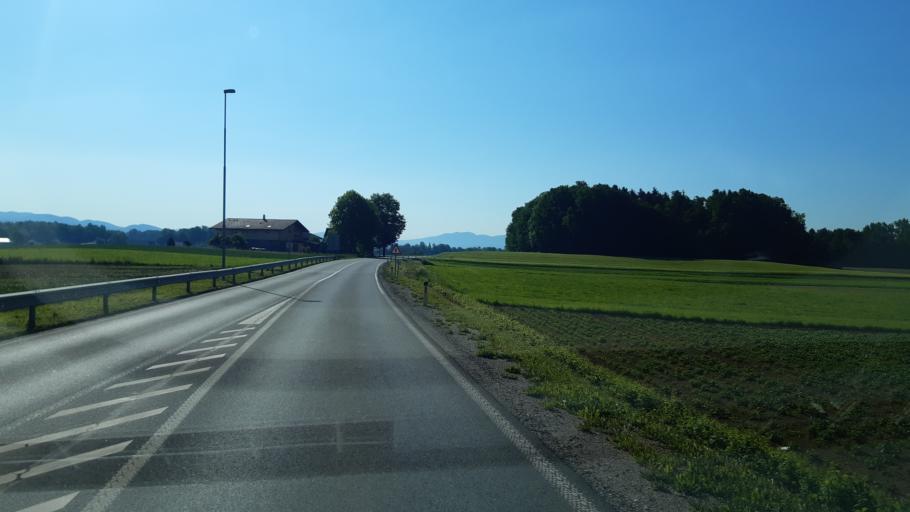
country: SI
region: Komenda
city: Komenda
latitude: 46.2016
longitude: 14.5328
